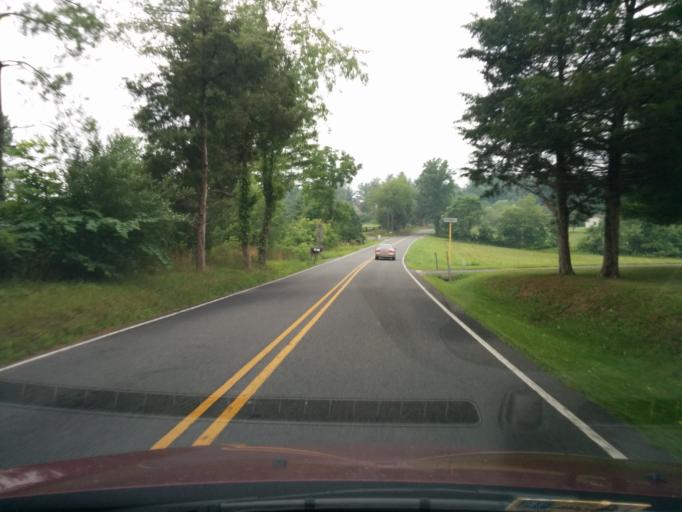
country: US
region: Virginia
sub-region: Rockbridge County
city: East Lexington
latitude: 37.8217
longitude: -79.4181
